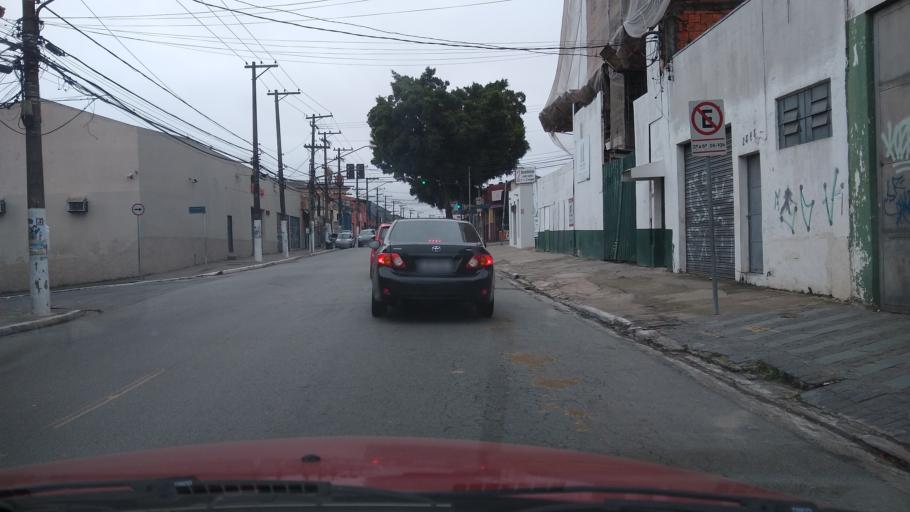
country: BR
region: Sao Paulo
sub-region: Diadema
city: Diadema
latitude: -23.6355
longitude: -46.6273
